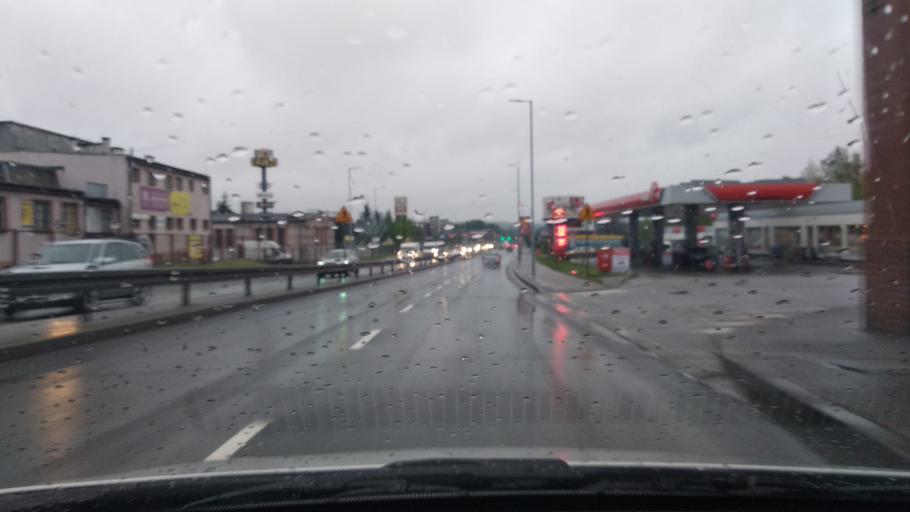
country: PL
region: Silesian Voivodeship
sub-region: Katowice
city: Katowice
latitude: 50.2601
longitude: 18.9858
